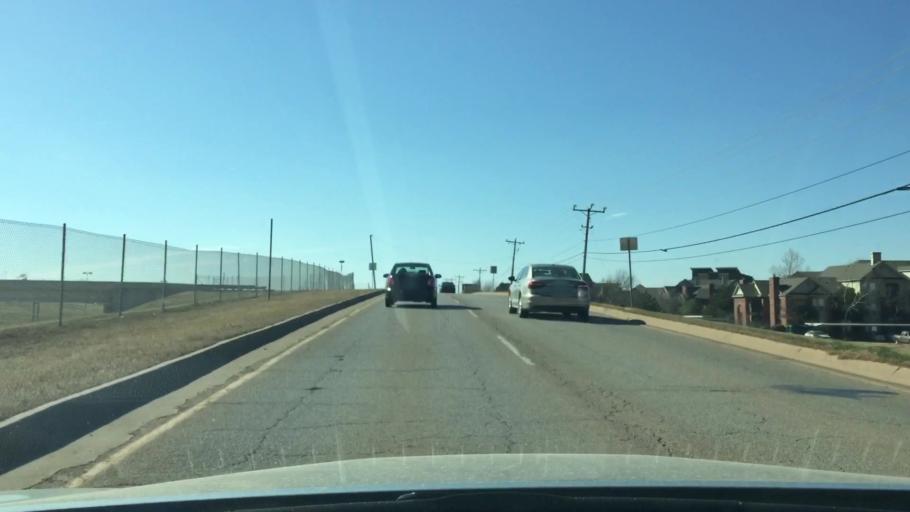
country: US
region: Oklahoma
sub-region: Oklahoma County
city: The Village
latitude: 35.6103
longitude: -97.5928
